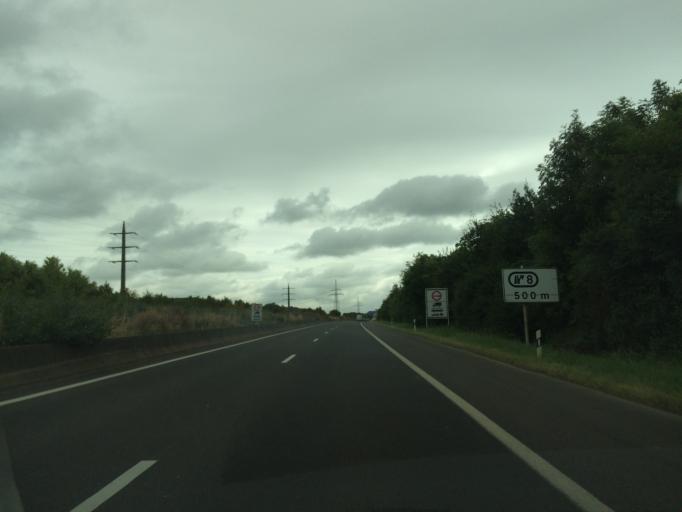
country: LU
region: Luxembourg
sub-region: Canton d'Esch-sur-Alzette
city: Dudelange
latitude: 49.5000
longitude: 6.0740
